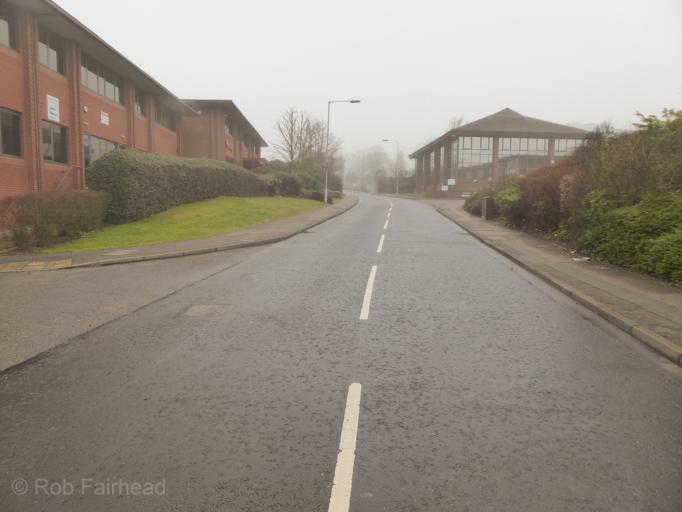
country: GB
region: England
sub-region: Hertfordshire
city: Letchworth Garden City
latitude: 51.9814
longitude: -0.2108
